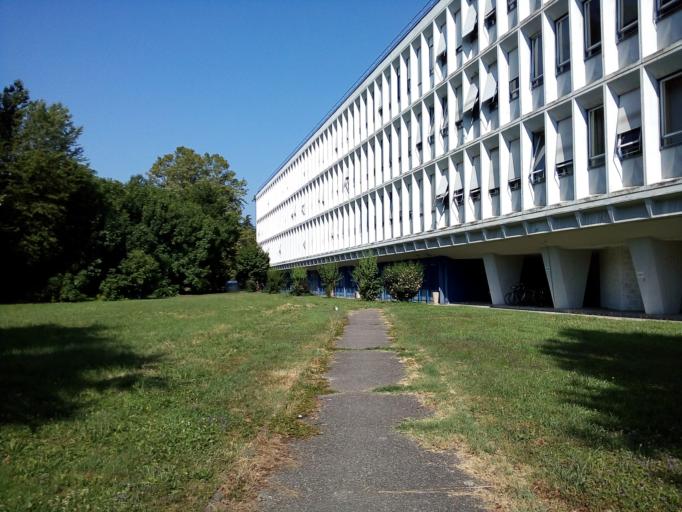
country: FR
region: Rhone-Alpes
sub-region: Departement de l'Isere
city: Corenc
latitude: 45.1952
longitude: 5.7715
